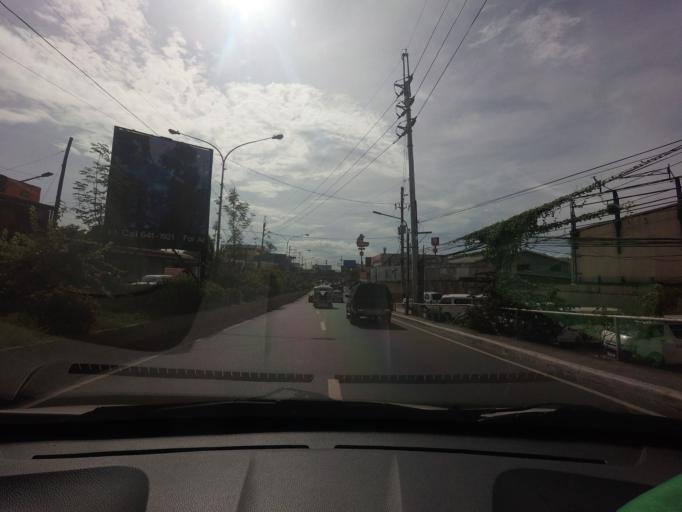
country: PH
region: Metro Manila
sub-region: Pasig
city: Pasig City
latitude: 14.5661
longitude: 121.0747
